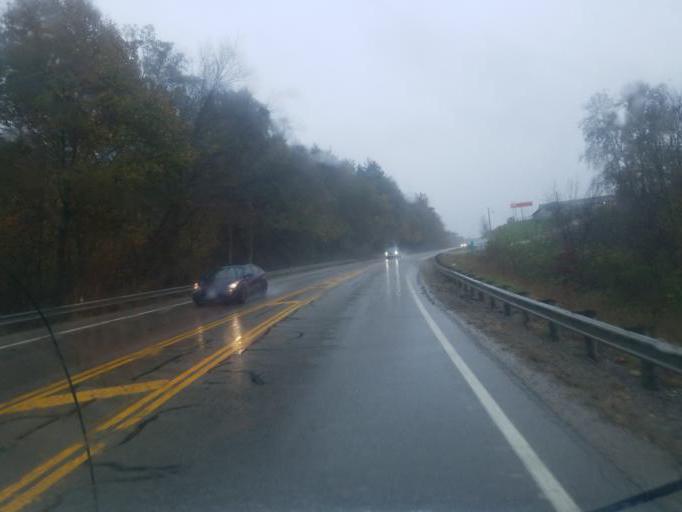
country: US
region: Ohio
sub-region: Muskingum County
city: North Zanesville
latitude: 39.9827
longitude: -82.0529
